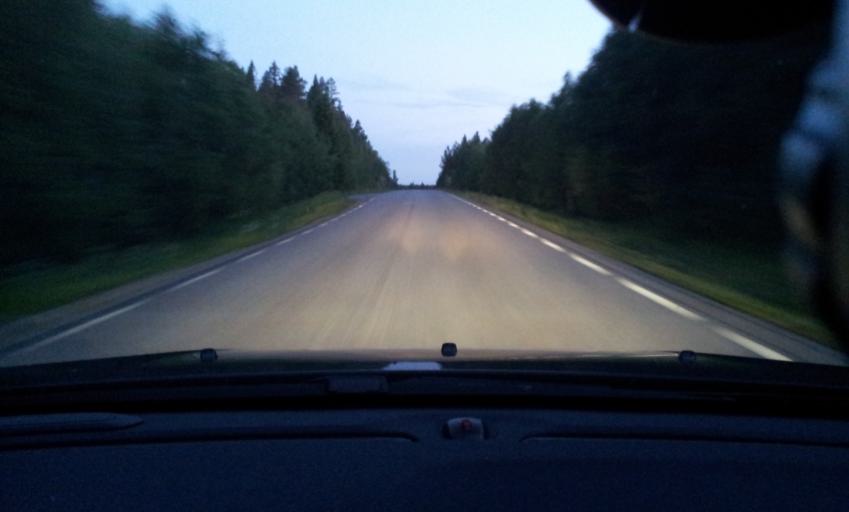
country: SE
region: Jaemtland
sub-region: Braecke Kommun
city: Braecke
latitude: 62.7412
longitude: 15.2074
